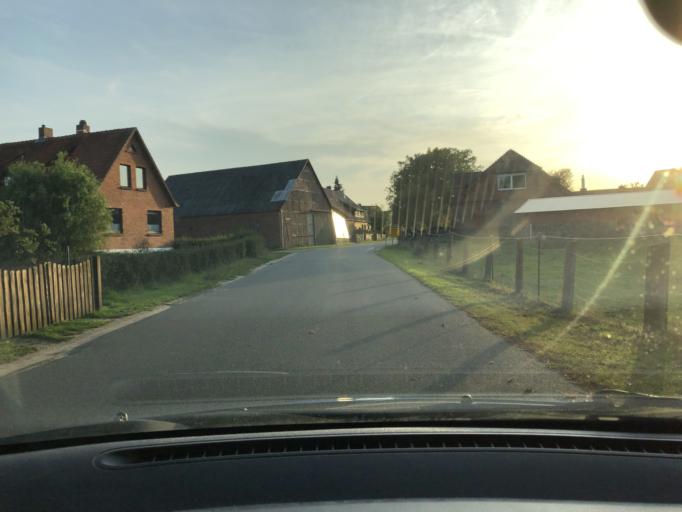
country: DE
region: Lower Saxony
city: Gohrde
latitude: 53.1415
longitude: 10.9586
